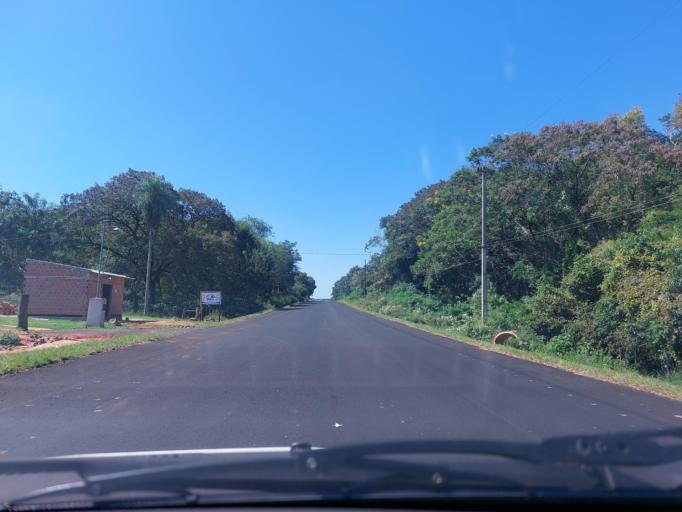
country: PY
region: San Pedro
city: Guayaybi
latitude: -24.5503
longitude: -56.4979
